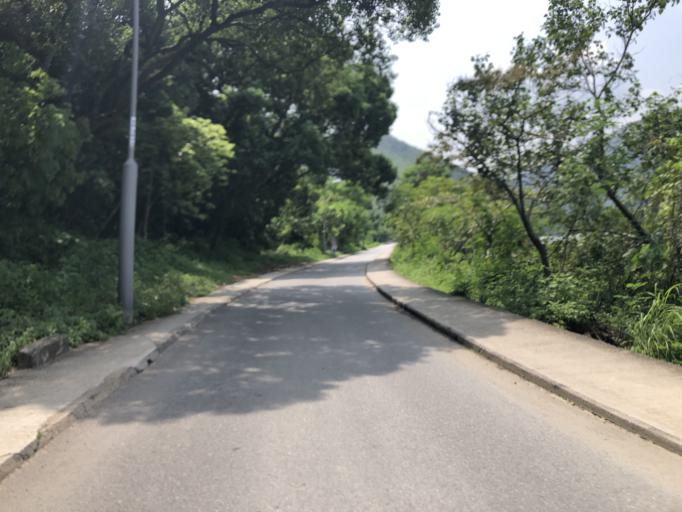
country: CN
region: Guangdong
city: Shatoujiao
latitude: 22.5252
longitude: 114.2136
